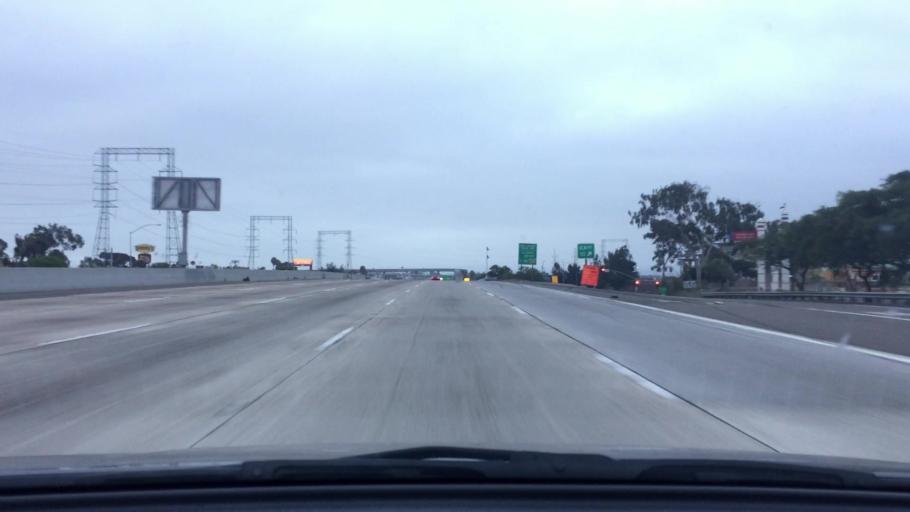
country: US
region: California
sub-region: San Diego County
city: National City
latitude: 32.6619
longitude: -117.1090
